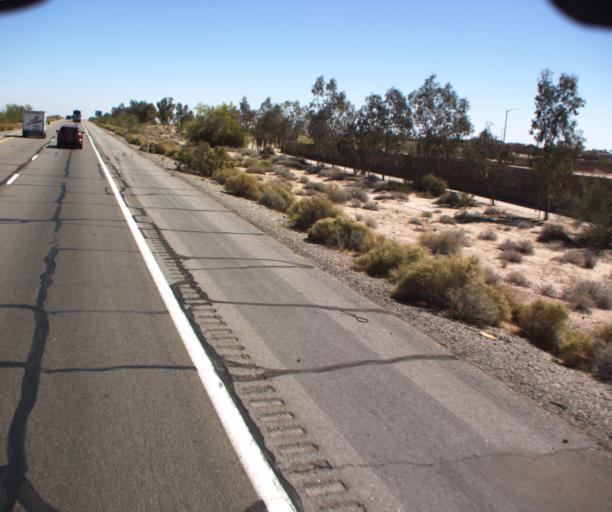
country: US
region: Arizona
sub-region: Yuma County
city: Wellton
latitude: 32.6537
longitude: -114.1759
